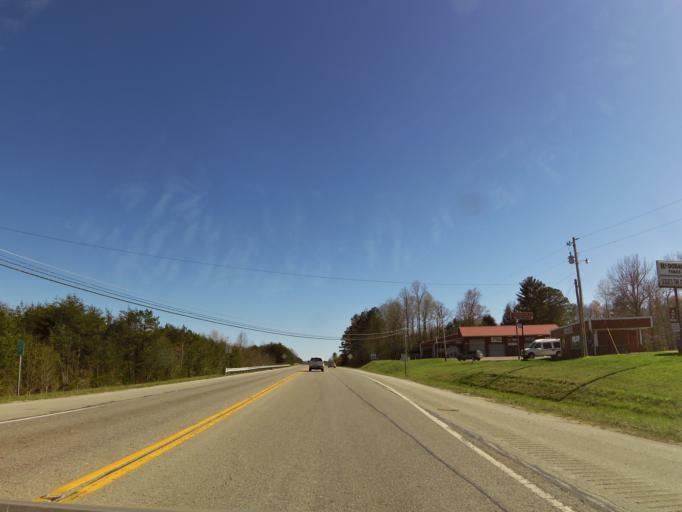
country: US
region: Kentucky
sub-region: McCreary County
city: Stearns
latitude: 36.6936
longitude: -84.4558
